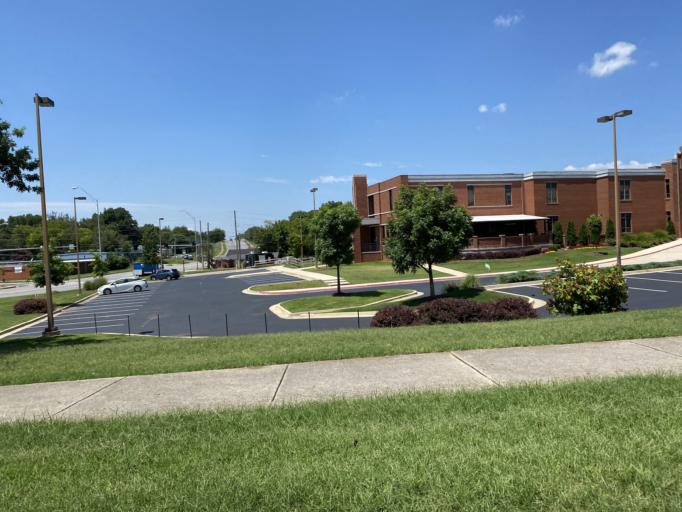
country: US
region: Alabama
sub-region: Madison County
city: Huntsville
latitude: 34.7202
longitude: -86.6084
